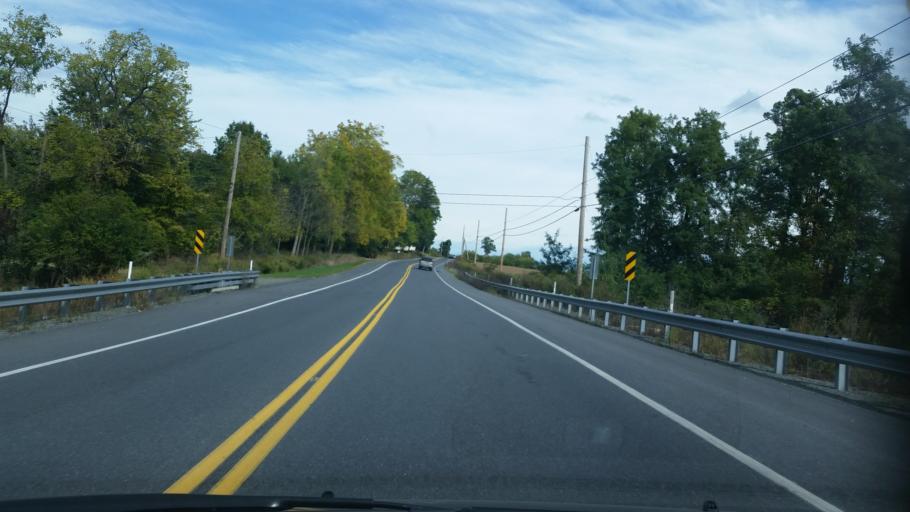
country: US
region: Pennsylvania
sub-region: Lehigh County
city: Breinigsville
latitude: 40.5556
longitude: -75.6485
